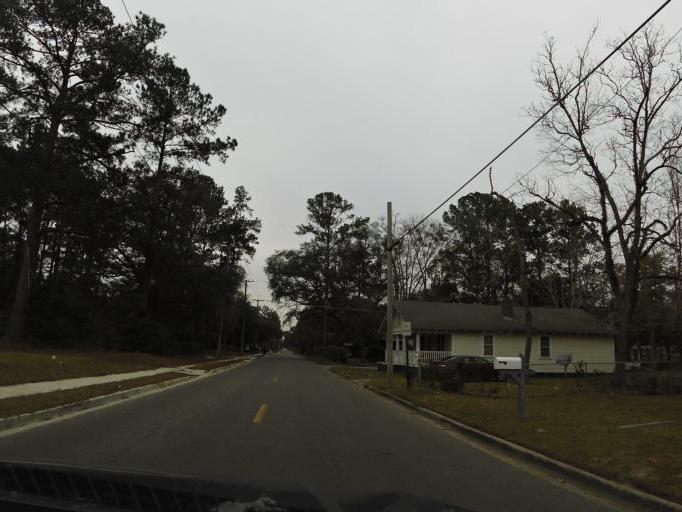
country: US
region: Georgia
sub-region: Thomas County
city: Thomasville
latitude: 30.8196
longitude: -83.9793
